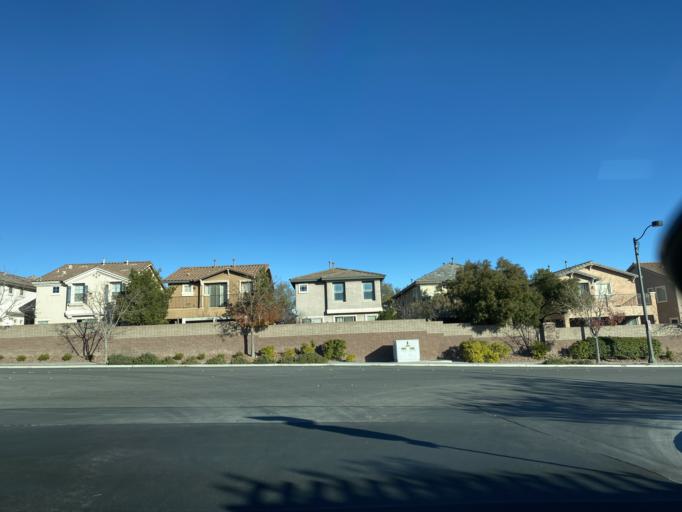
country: US
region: Nevada
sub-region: Clark County
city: Summerlin South
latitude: 36.2989
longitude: -115.3301
